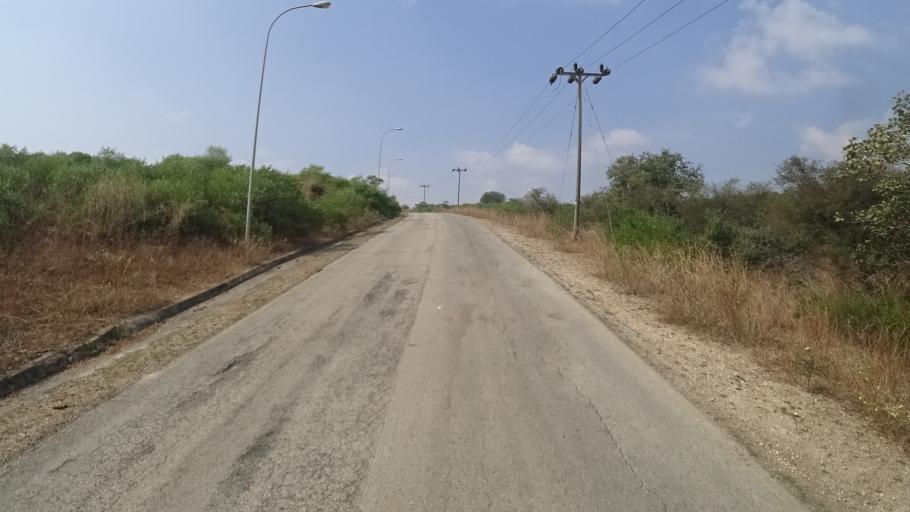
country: YE
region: Al Mahrah
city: Hawf
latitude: 16.7283
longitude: 53.2751
